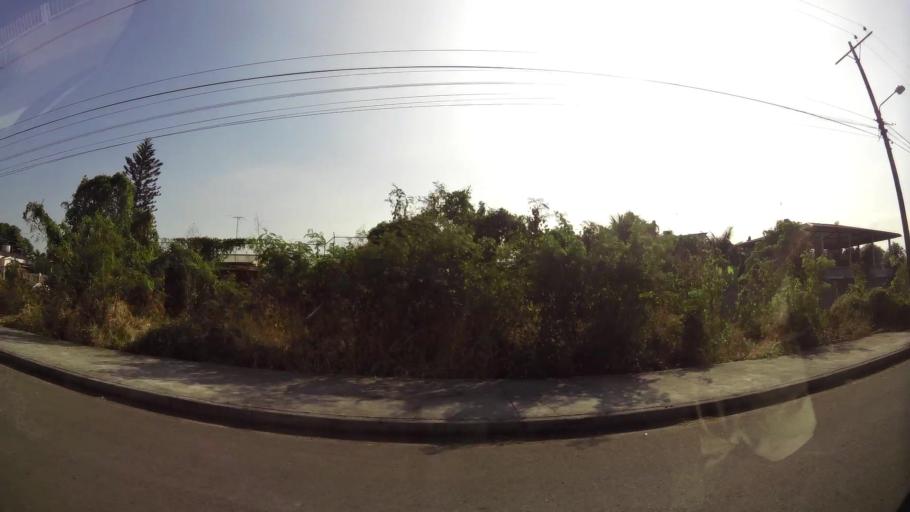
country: EC
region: Guayas
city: Eloy Alfaro
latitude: -2.2026
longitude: -79.8216
